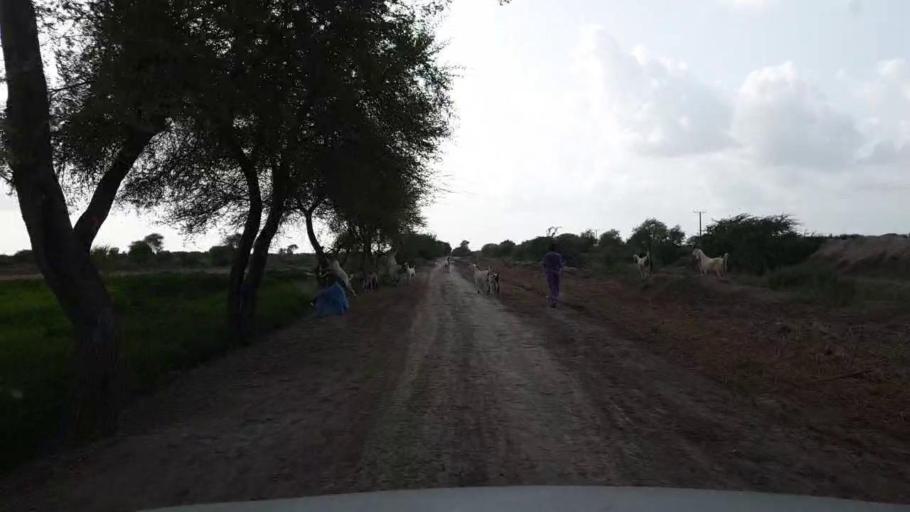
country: PK
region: Sindh
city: Kario
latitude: 24.7635
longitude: 68.6025
